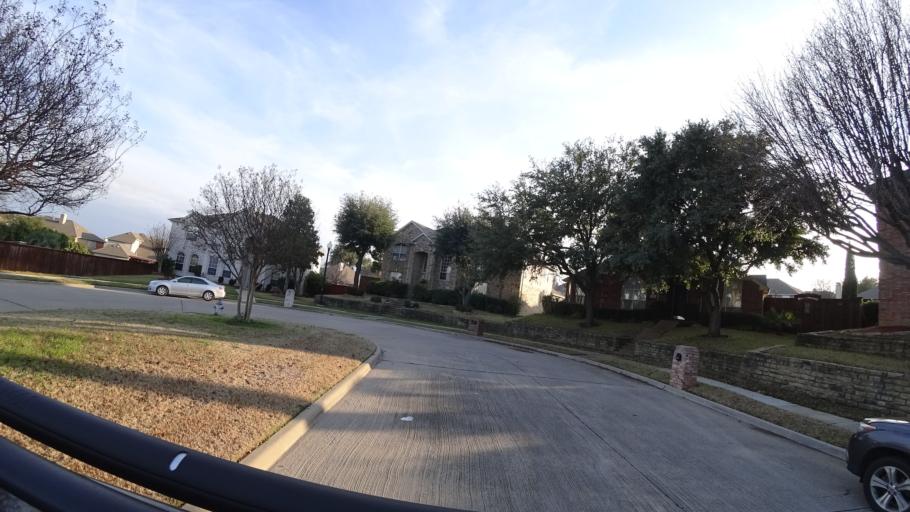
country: US
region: Texas
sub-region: Denton County
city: Lewisville
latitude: 32.9957
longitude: -96.9840
